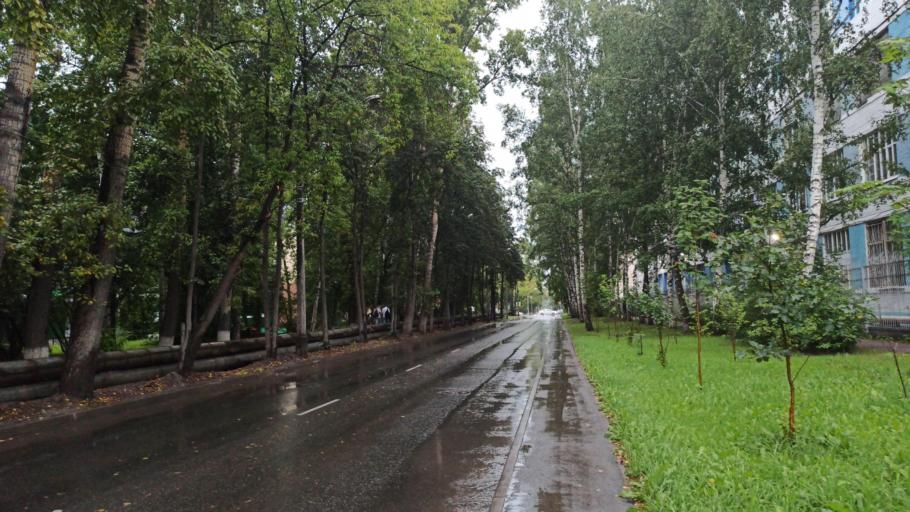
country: RU
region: Tomsk
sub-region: Tomskiy Rayon
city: Tomsk
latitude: 56.4624
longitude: 84.9629
